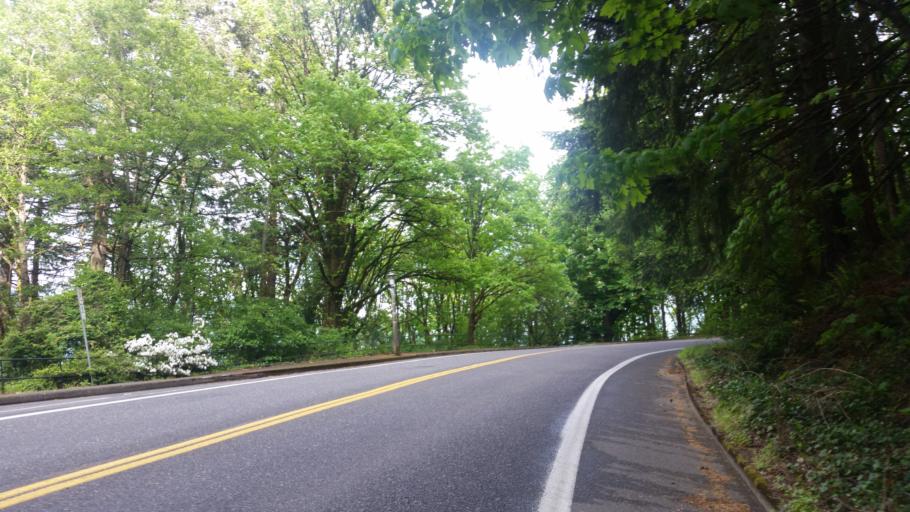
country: US
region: Oregon
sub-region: Multnomah County
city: Portland
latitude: 45.4863
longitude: -122.6844
